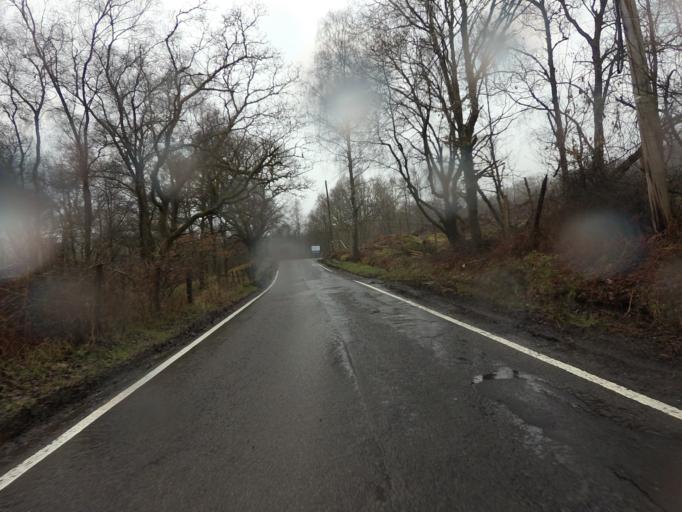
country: GB
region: Scotland
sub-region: Stirling
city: Killearn
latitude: 56.1900
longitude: -4.4983
